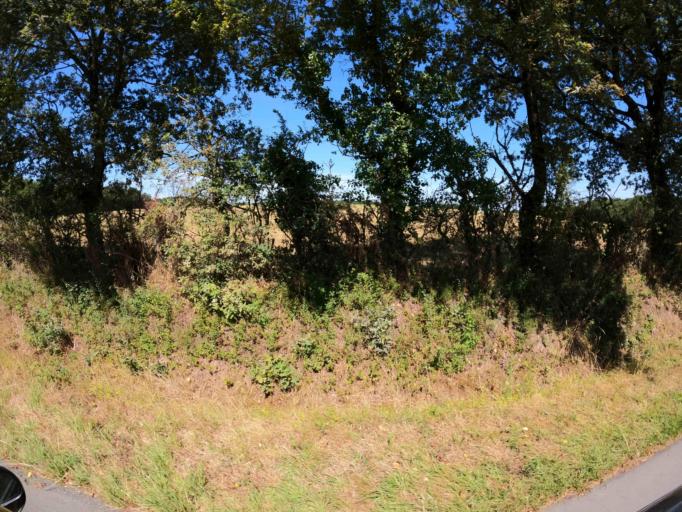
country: FR
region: Pays de la Loire
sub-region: Departement de la Loire-Atlantique
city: La Limouziniere
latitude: 46.9611
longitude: -1.5894
